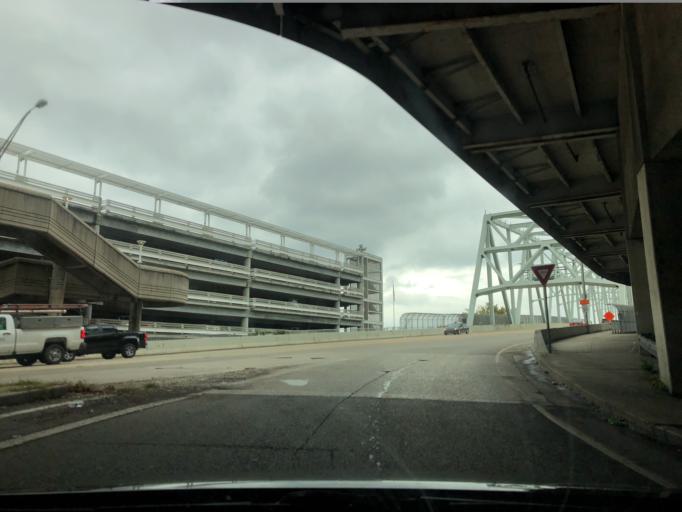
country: US
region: Kentucky
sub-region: Campbell County
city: Newport
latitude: 39.0986
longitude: -84.5043
